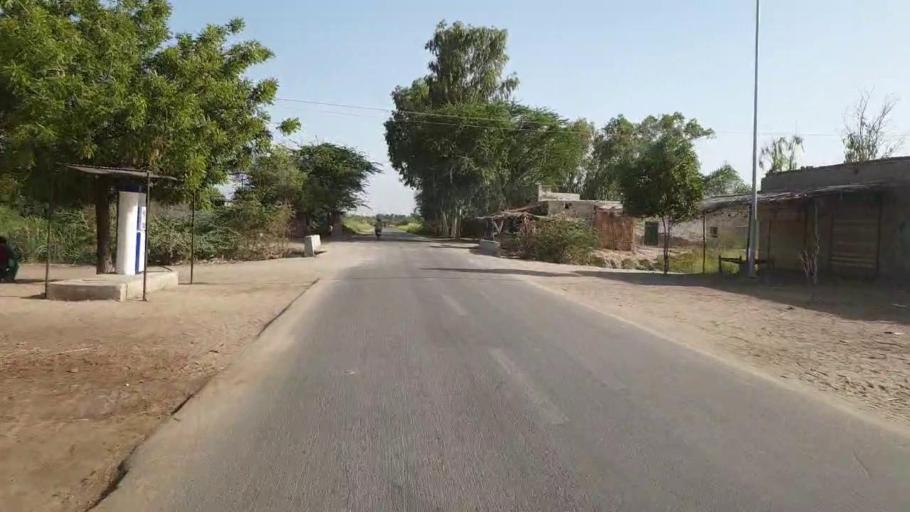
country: PK
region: Sindh
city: Daur
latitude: 26.4619
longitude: 68.4512
